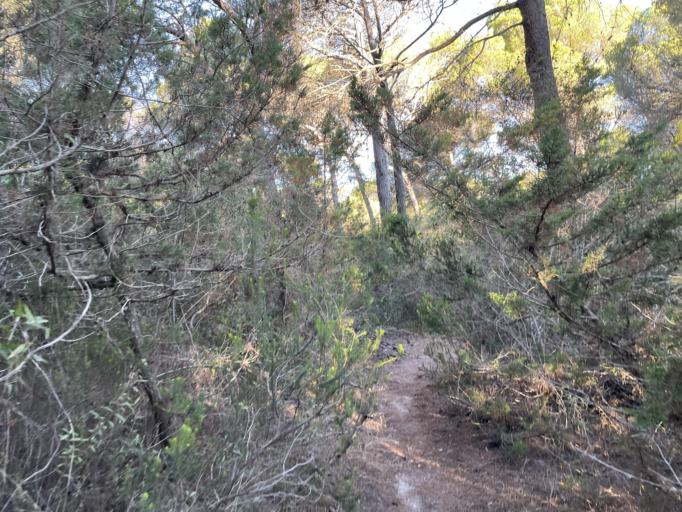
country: ES
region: Balearic Islands
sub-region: Illes Balears
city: Capdepera
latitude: 39.7184
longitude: 3.4542
